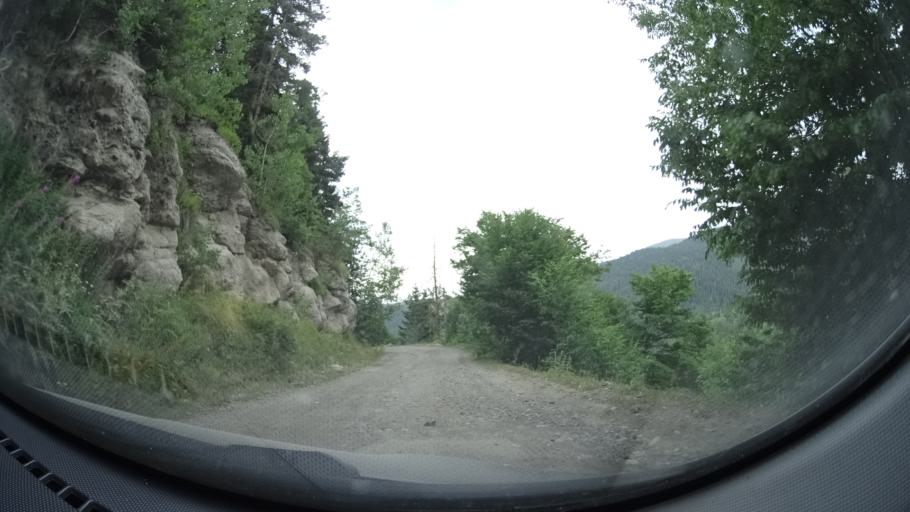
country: GE
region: Samtskhe-Javakheti
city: Adigeni
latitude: 41.6417
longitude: 42.5906
